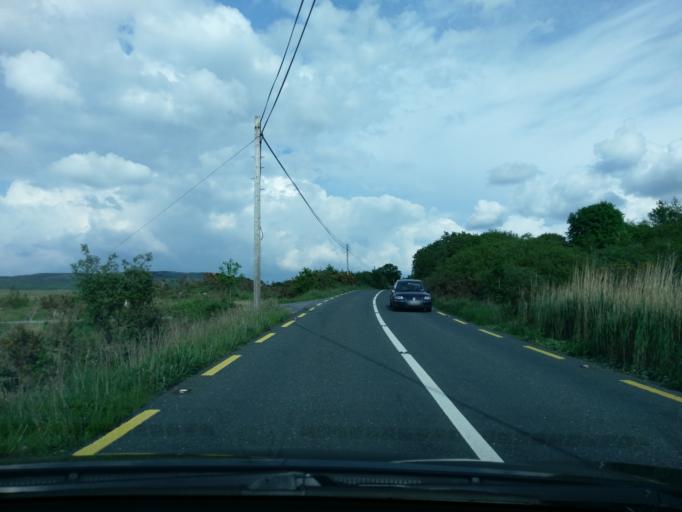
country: IE
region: Connaught
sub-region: County Galway
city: Oughterard
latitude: 53.4510
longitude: -9.4836
